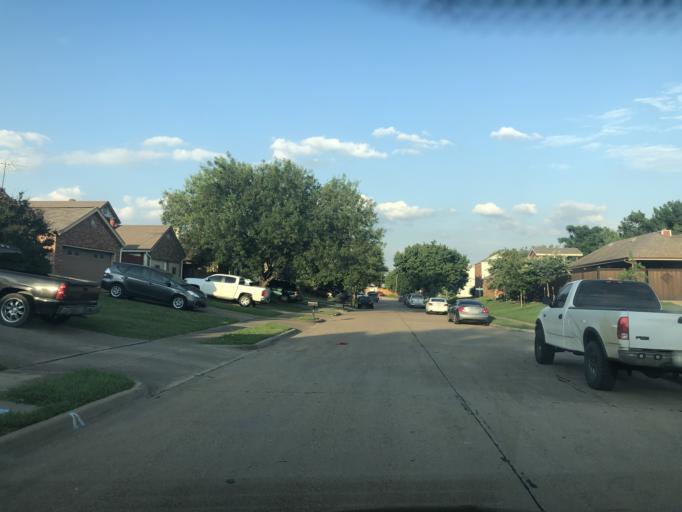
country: US
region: Texas
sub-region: Dallas County
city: Irving
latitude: 32.7853
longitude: -96.9622
